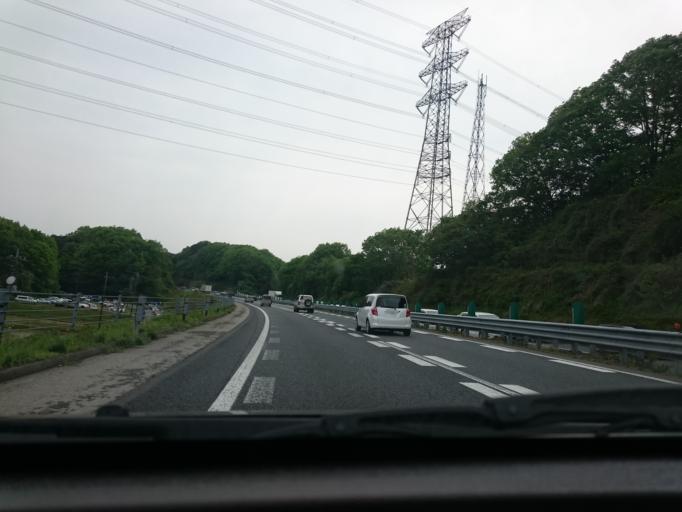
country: JP
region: Tochigi
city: Utsunomiya-shi
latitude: 36.6632
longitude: 139.8653
